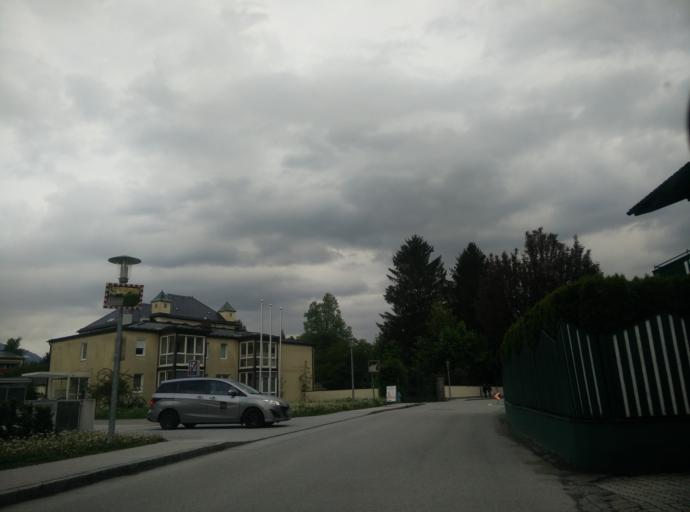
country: AT
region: Salzburg
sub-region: Politischer Bezirk Hallein
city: Oberalm
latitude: 47.7036
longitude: 13.0889
